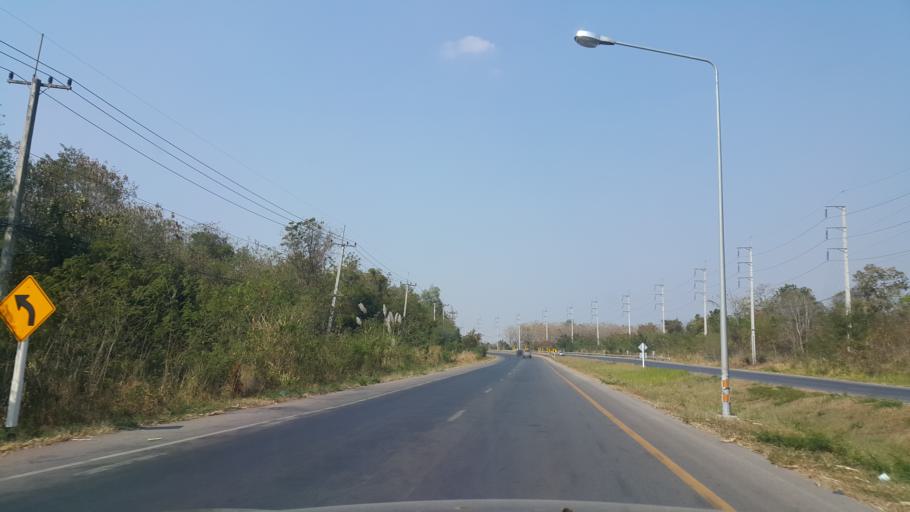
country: TH
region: Chaiyaphum
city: Phu Khiao
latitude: 16.4133
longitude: 102.1322
